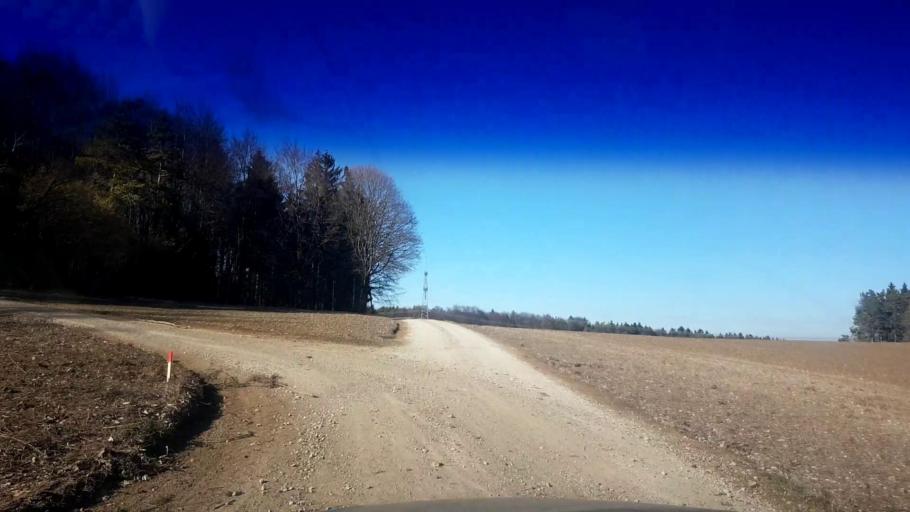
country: DE
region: Bavaria
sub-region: Upper Franconia
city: Poxdorf
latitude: 49.9624
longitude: 11.0864
